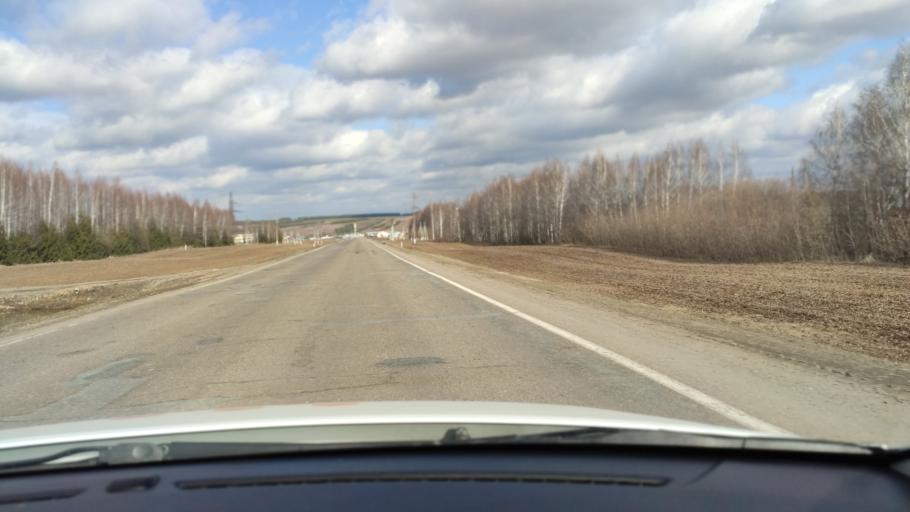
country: RU
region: Tatarstan
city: Vysokaya Gora
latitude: 56.1146
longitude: 49.1893
